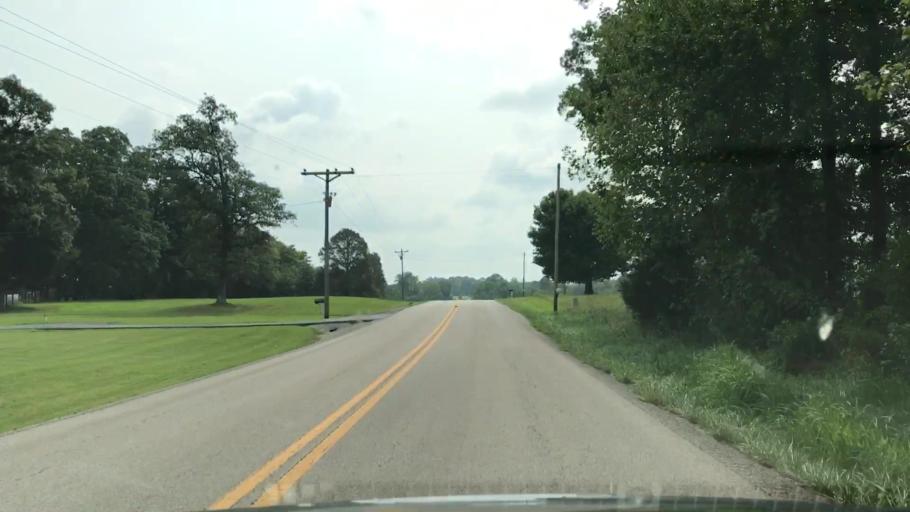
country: US
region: Kentucky
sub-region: Edmonson County
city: Brownsville
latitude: 37.1440
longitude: -86.1917
